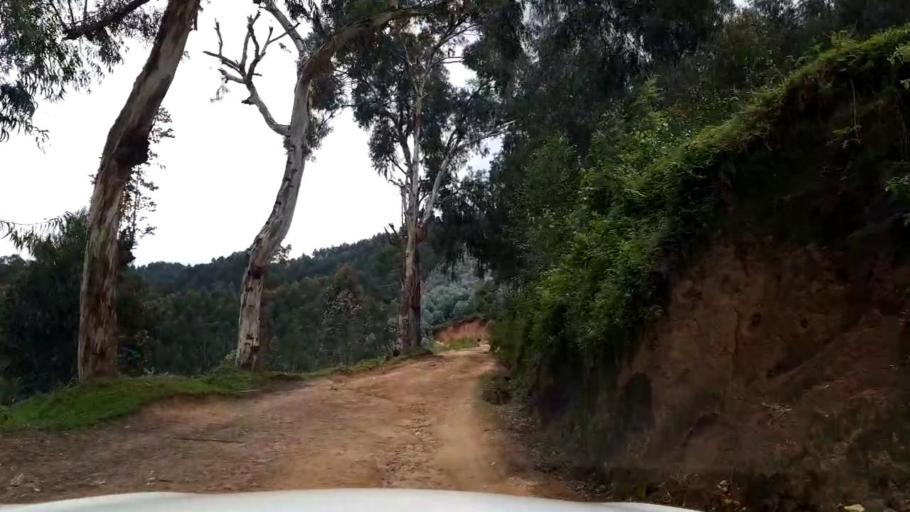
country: RW
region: Western Province
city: Kibuye
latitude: -1.9609
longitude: 29.3947
